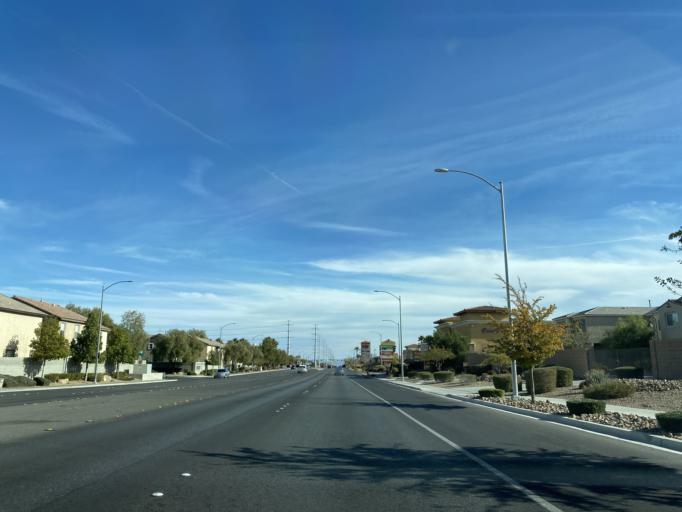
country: US
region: Nevada
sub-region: Clark County
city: Enterprise
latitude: 36.0554
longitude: -115.2846
